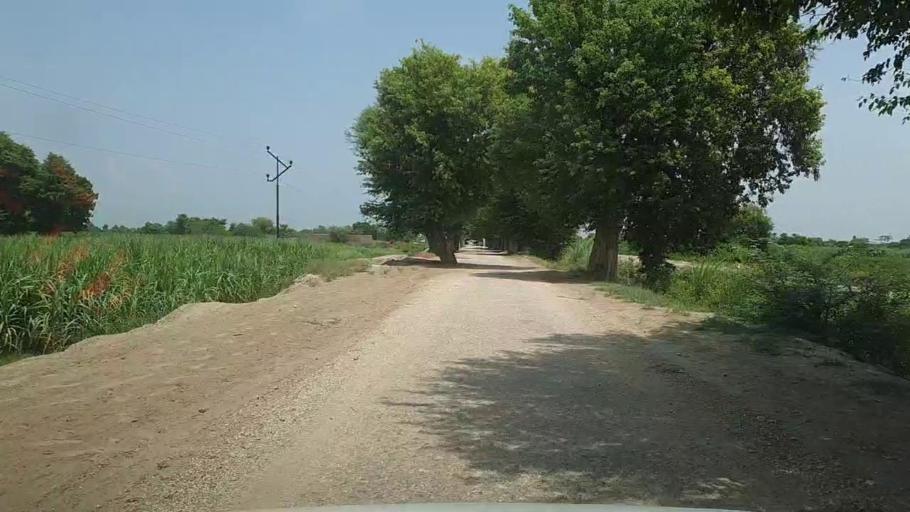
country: PK
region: Sindh
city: Karaundi
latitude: 26.9146
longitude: 68.3374
